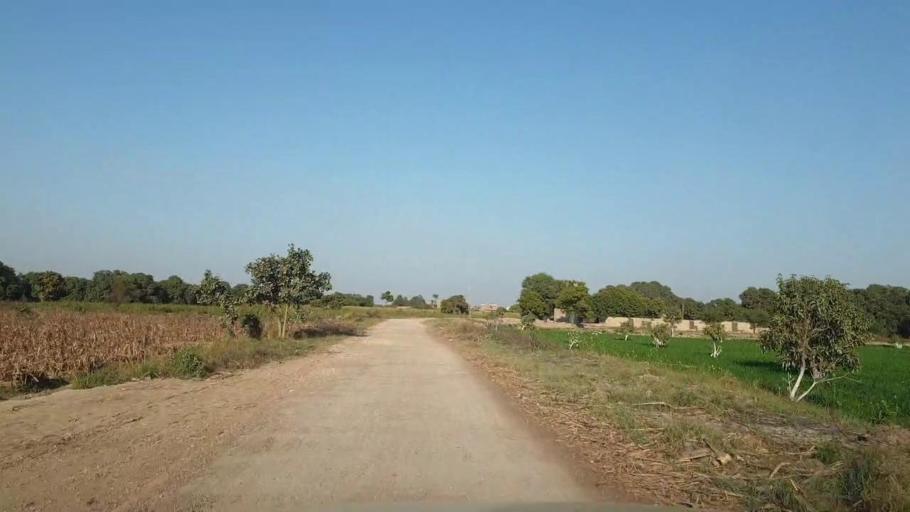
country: PK
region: Sindh
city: Tando Allahyar
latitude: 25.4908
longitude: 68.6414
